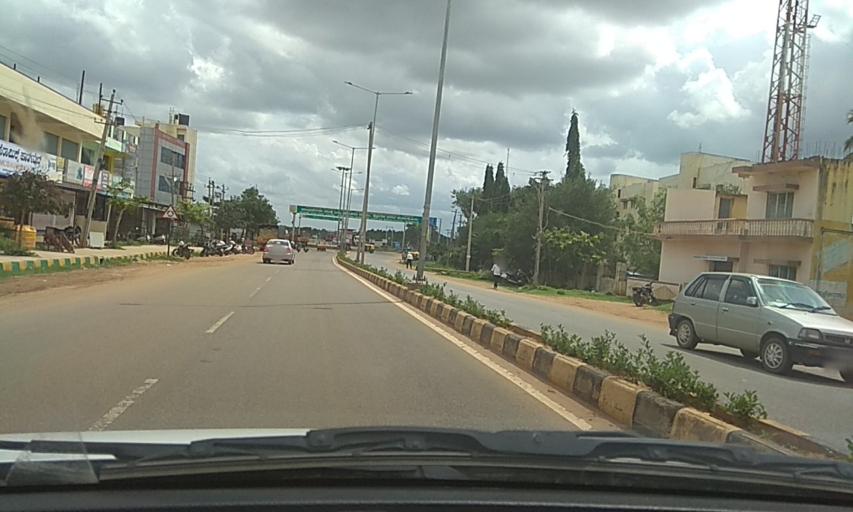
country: IN
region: Karnataka
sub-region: Tumkur
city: Tumkur
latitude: 13.3172
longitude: 77.0915
